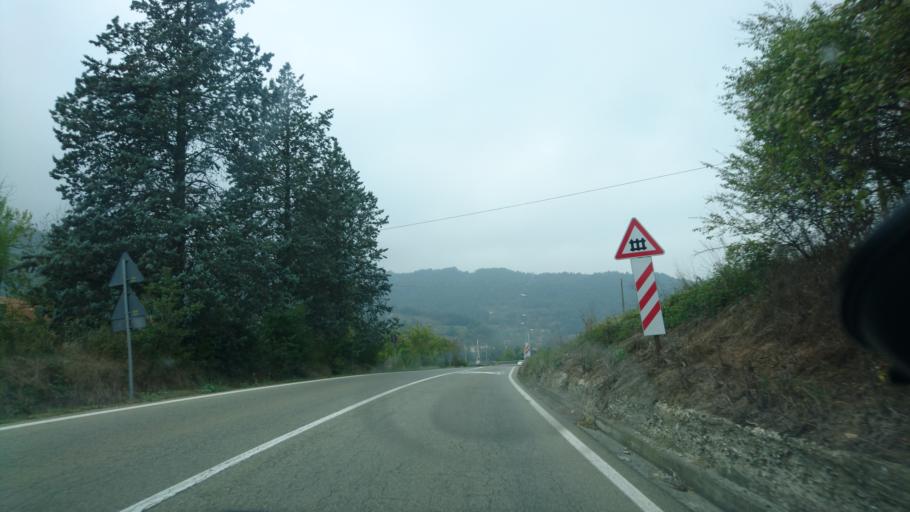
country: IT
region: Piedmont
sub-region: Provincia di Alessandria
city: Ponti
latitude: 44.6129
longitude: 8.3502
